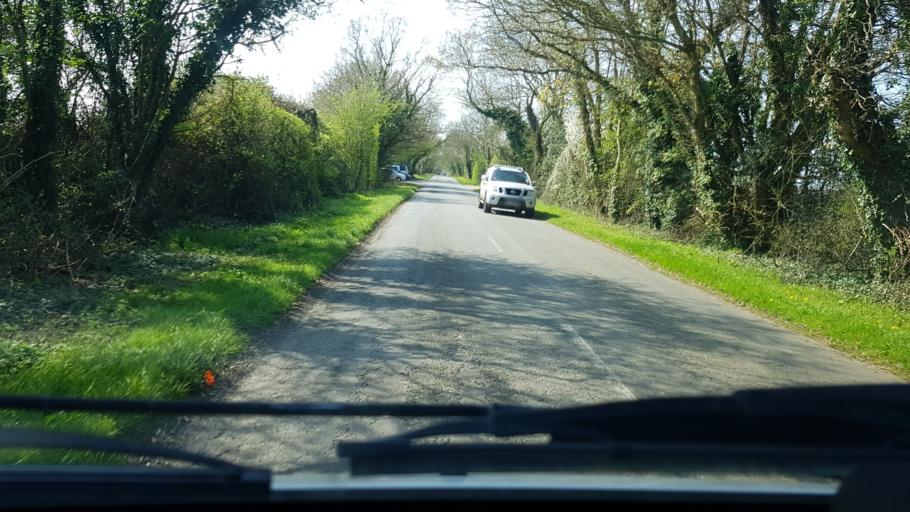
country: GB
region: England
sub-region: West Sussex
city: Chichester
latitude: 50.8626
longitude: -0.7886
